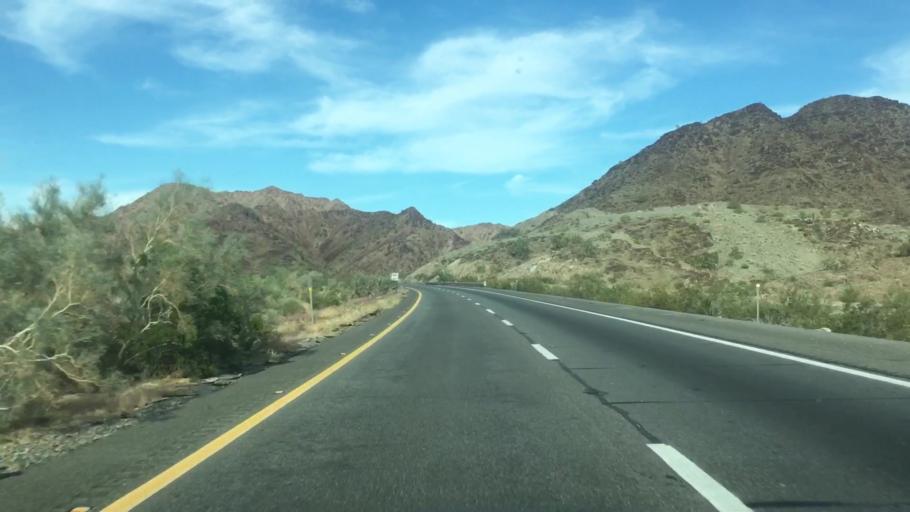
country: US
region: Arizona
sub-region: La Paz County
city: Ehrenberg
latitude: 33.6384
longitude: -114.3866
